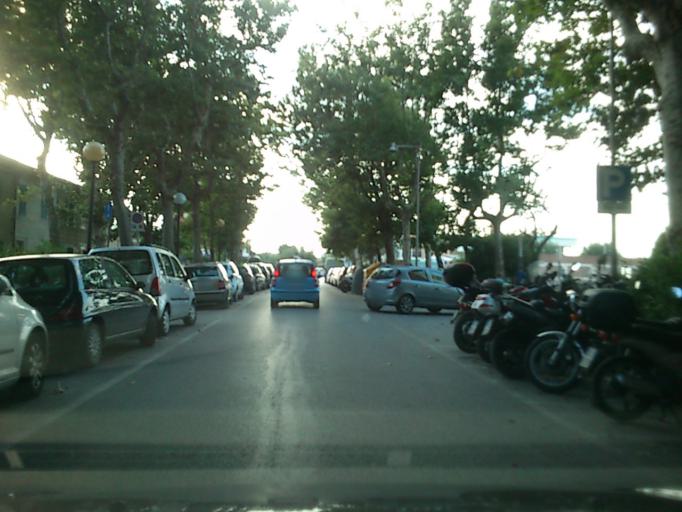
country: IT
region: The Marches
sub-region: Provincia di Pesaro e Urbino
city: Fano
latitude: 43.8505
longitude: 13.0124
